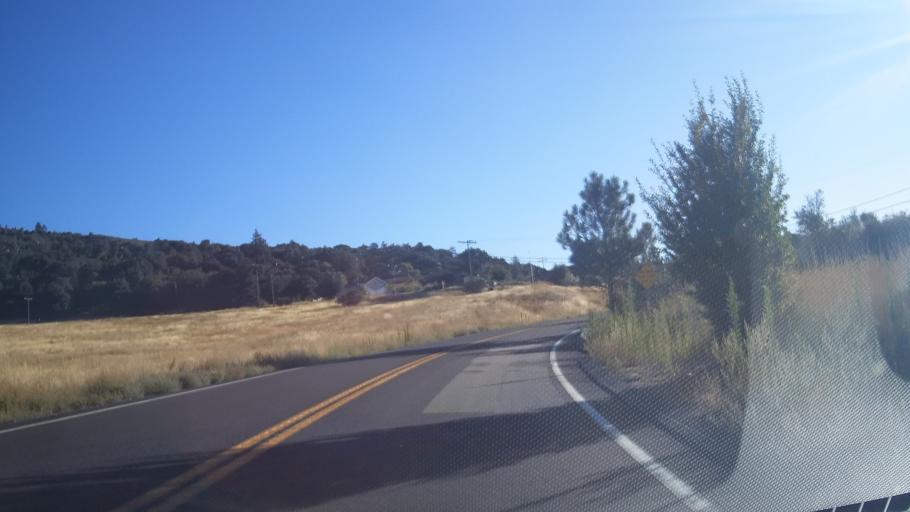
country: US
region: California
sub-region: San Diego County
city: Julian
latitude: 32.9916
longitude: -116.5878
